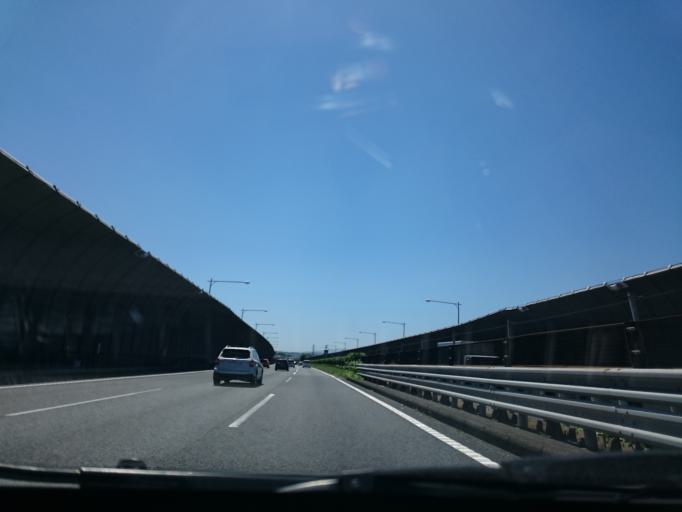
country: JP
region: Kanagawa
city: Isehara
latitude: 35.3997
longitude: 139.2874
